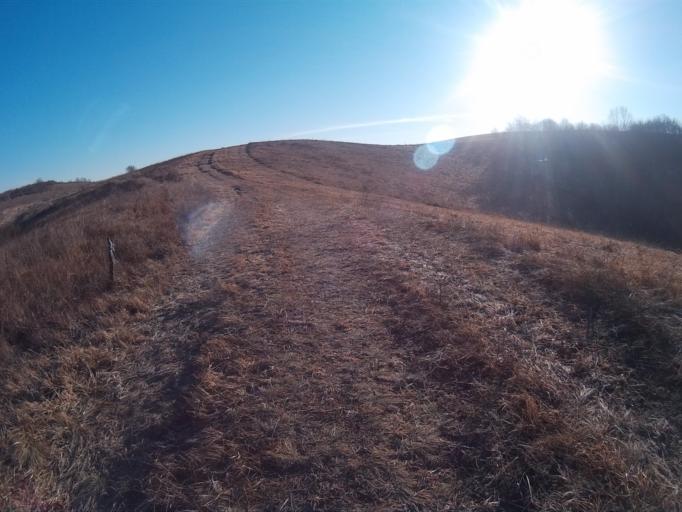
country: HU
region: Borsod-Abauj-Zemplen
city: Putnok
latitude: 48.3756
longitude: 20.4433
